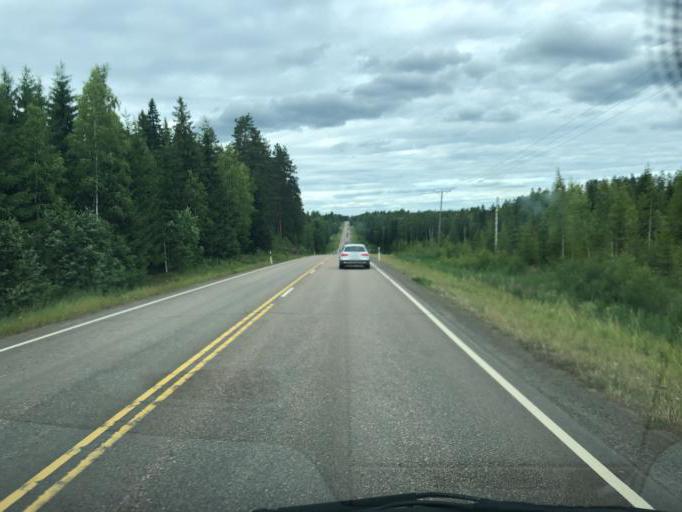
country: FI
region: Southern Savonia
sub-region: Mikkeli
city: Maentyharju
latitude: 61.0744
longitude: 27.0594
